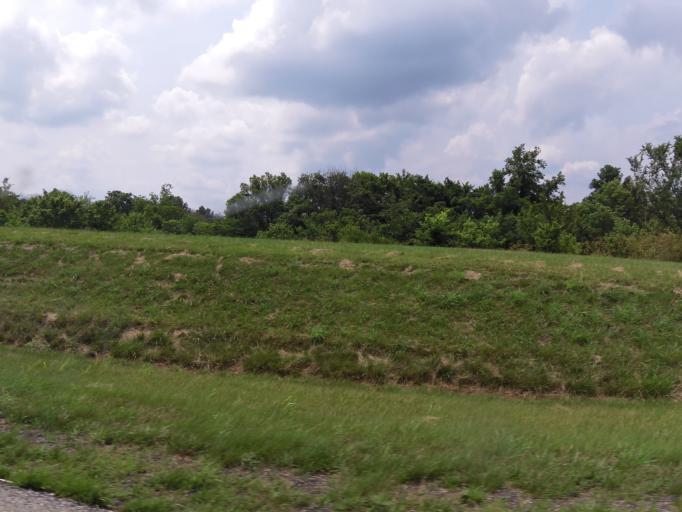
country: US
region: Kentucky
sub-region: Trimble County
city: Providence
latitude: 38.4871
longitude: -85.2631
